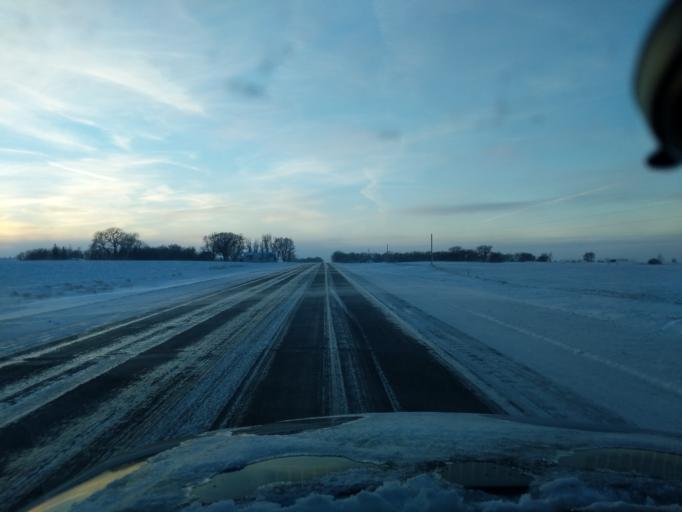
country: US
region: Minnesota
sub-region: Renville County
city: Renville
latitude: 44.7889
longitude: -95.2655
